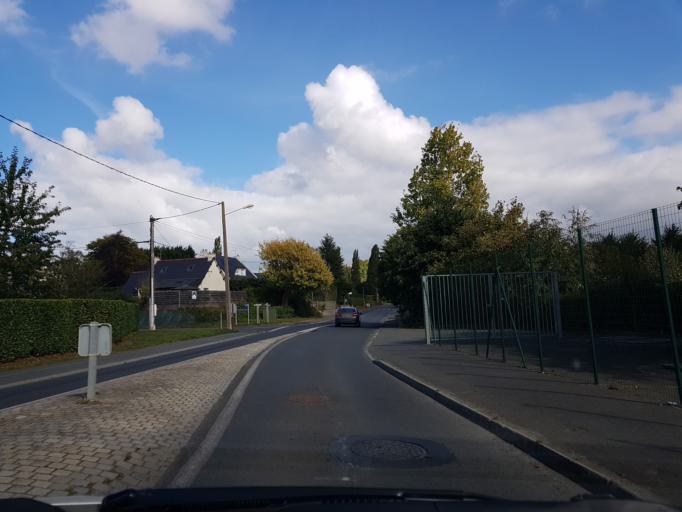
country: FR
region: Brittany
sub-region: Departement des Cotes-d'Armor
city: Pledran
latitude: 48.4711
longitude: -2.7605
